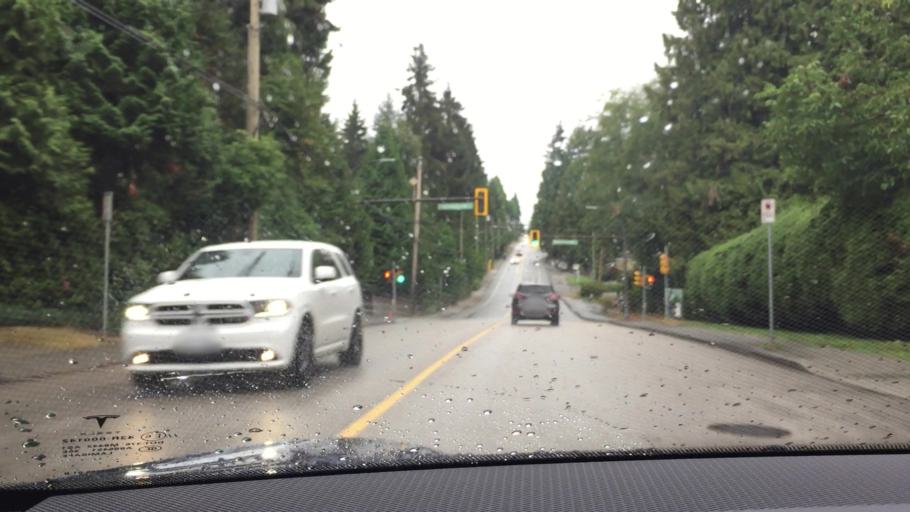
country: CA
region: British Columbia
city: Burnaby
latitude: 49.2343
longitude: -122.9567
